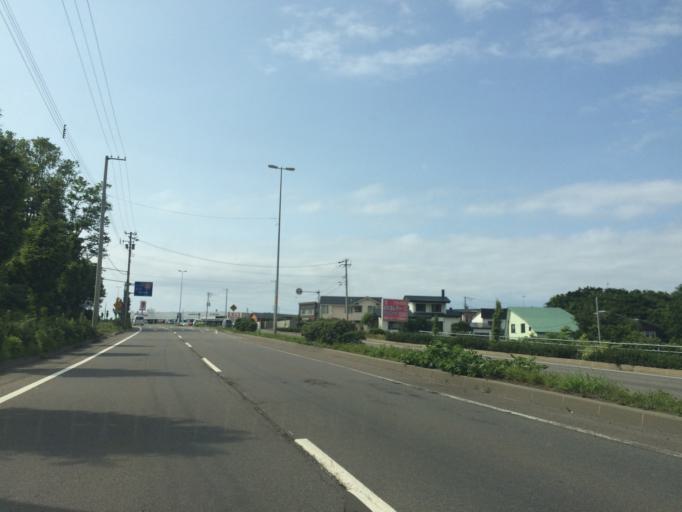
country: JP
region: Hokkaido
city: Otaru
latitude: 43.2095
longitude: 140.9206
